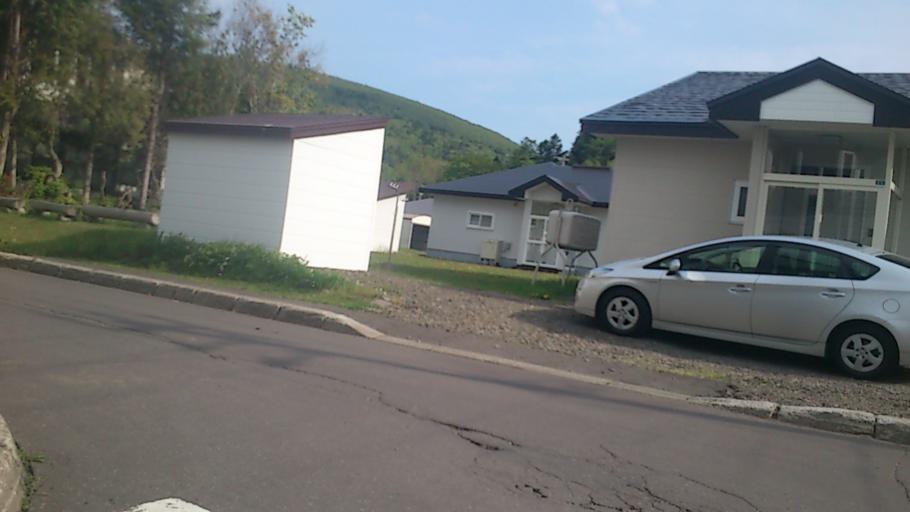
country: JP
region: Hokkaido
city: Bihoro
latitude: 43.4322
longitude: 144.0965
